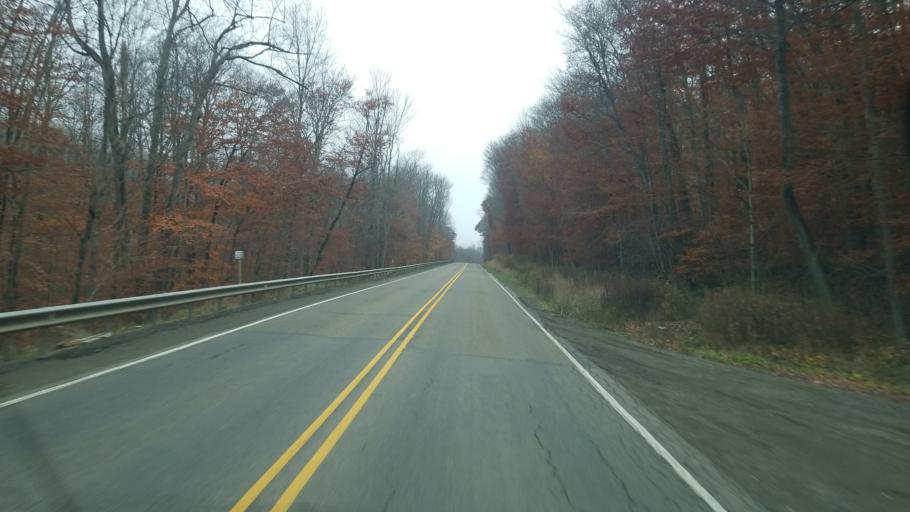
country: US
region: Pennsylvania
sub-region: McKean County
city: Smethport
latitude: 41.8099
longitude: -78.4957
